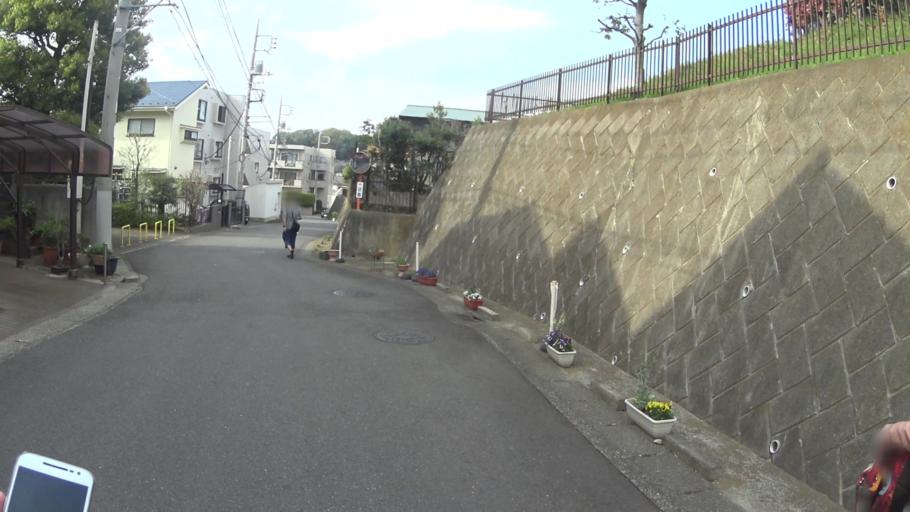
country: JP
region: Tokyo
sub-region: Machida-shi
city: Machida
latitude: 35.5805
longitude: 139.4888
